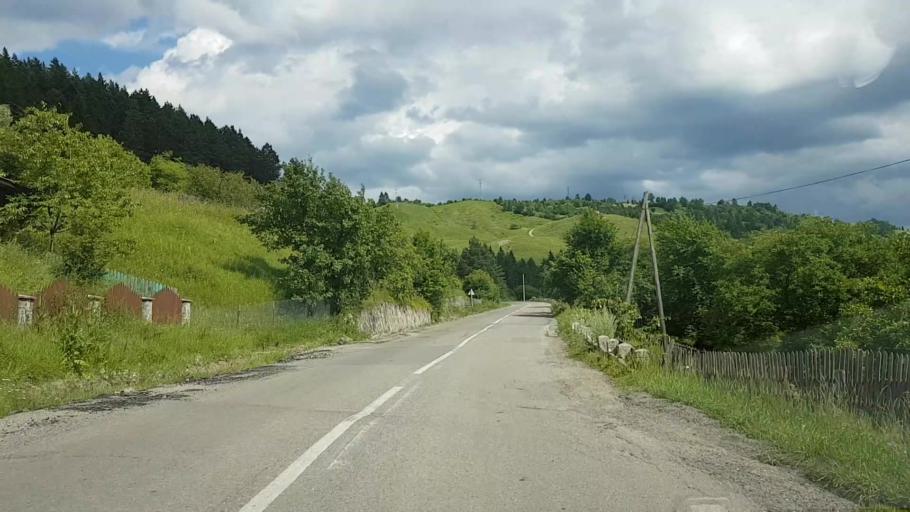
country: RO
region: Neamt
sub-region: Comuna Hangu
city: Hangu
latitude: 47.0071
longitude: 26.0922
